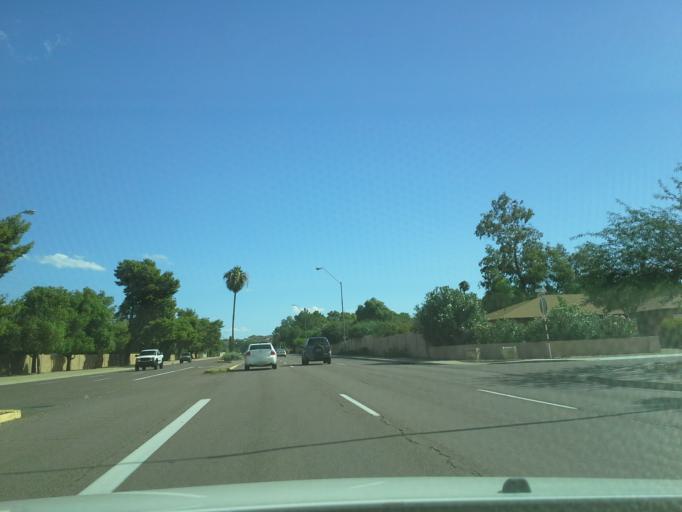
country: US
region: Arizona
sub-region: Maricopa County
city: Glendale
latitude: 33.6076
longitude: -112.0727
